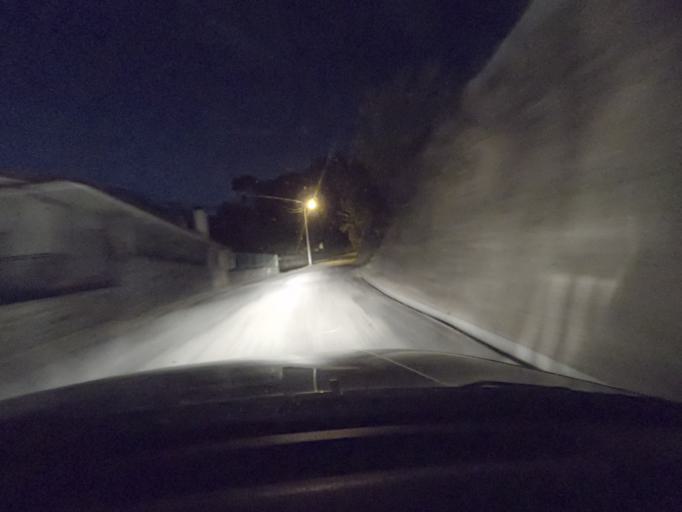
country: PT
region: Vila Real
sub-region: Santa Marta de Penaguiao
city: Santa Marta de Penaguiao
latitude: 41.2208
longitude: -7.8410
